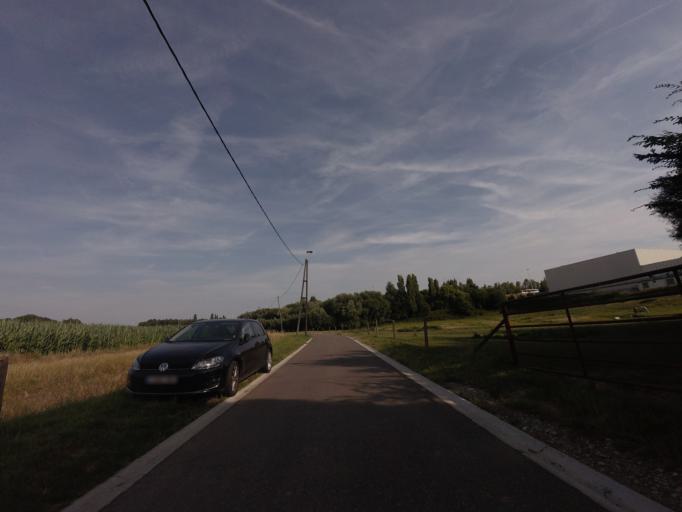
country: BE
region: Flanders
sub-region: Provincie Vlaams-Brabant
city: Meise
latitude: 50.9185
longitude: 4.3471
